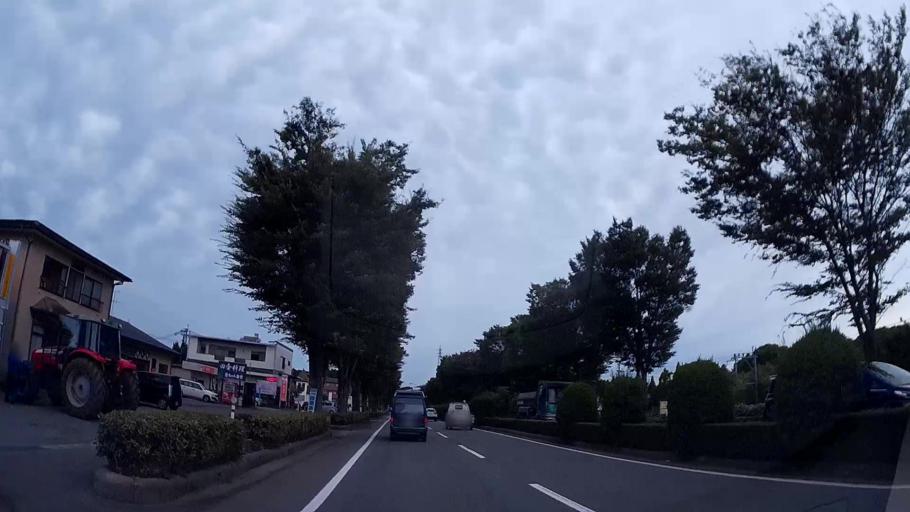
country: JP
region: Kumamoto
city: Ozu
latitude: 32.8992
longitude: 130.8531
